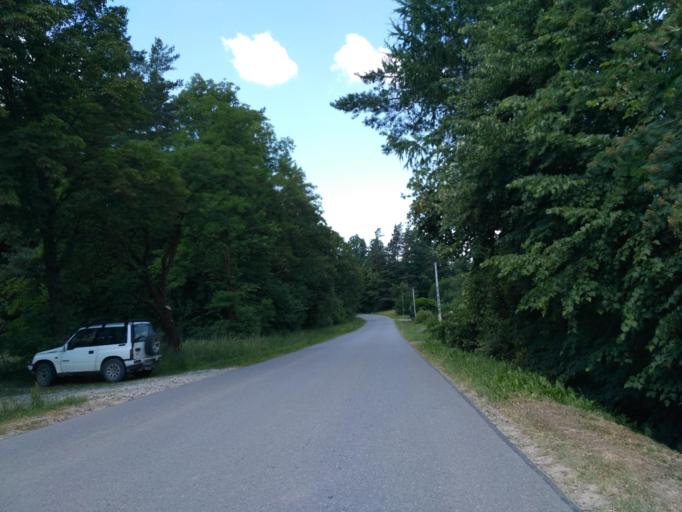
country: PL
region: Subcarpathian Voivodeship
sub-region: Powiat sanocki
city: Niebieszczany
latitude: 49.4877
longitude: 22.1878
